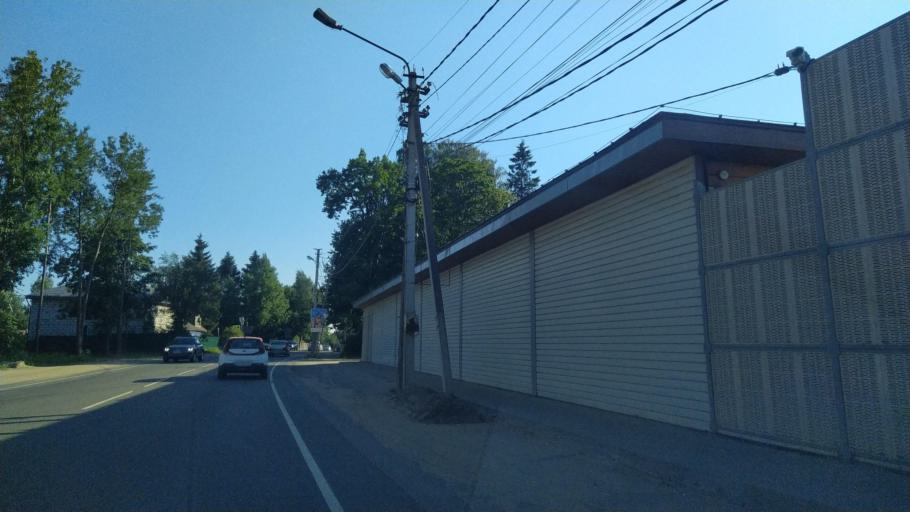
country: RU
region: Leningrad
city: Toksovo
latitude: 60.1633
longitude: 30.5393
